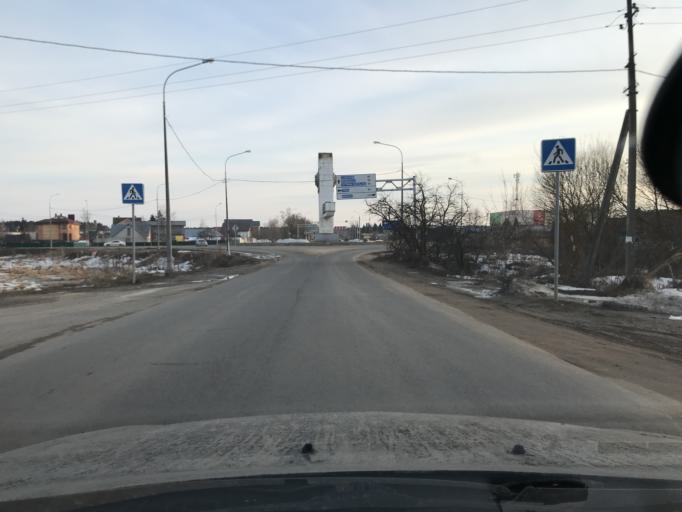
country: RU
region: Kaluga
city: Kaluga
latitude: 54.4699
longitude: 36.2408
